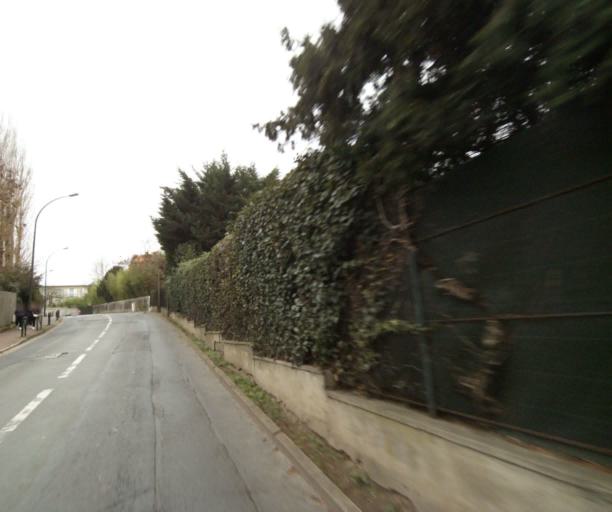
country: FR
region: Ile-de-France
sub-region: Departement des Hauts-de-Seine
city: Saint-Cloud
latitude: 48.8520
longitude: 2.1932
